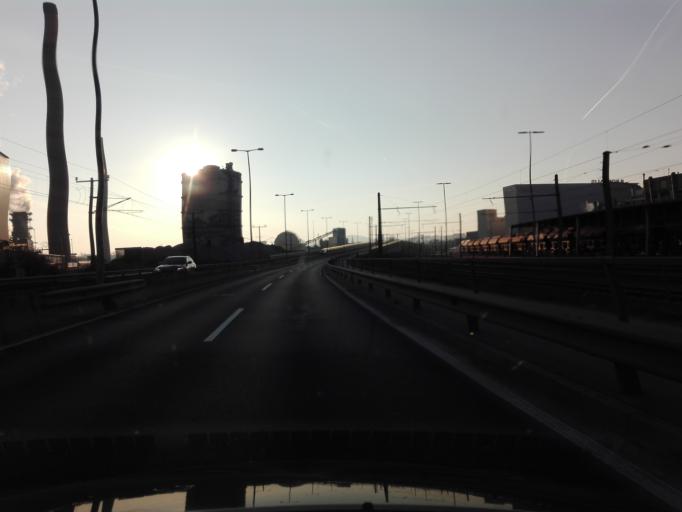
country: AT
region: Upper Austria
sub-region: Politischer Bezirk Urfahr-Umgebung
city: Steyregg
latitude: 48.2851
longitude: 14.3310
